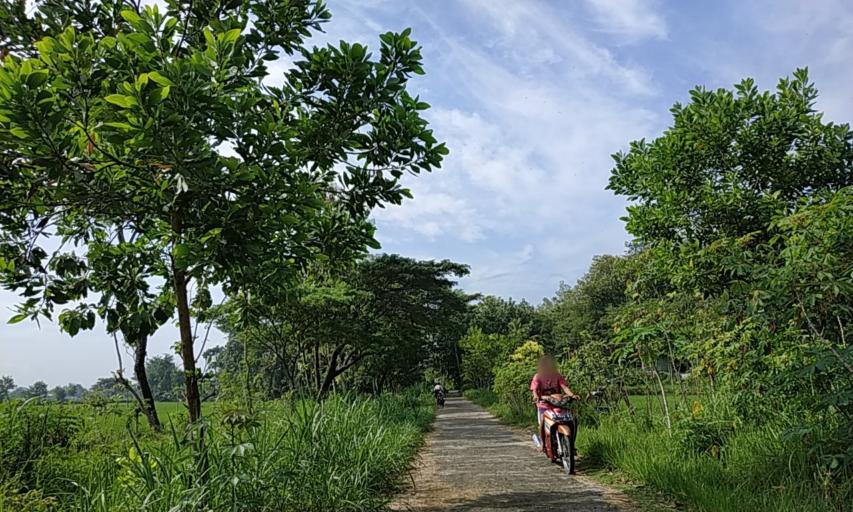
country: ID
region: Central Java
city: Trucuk
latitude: -7.7636
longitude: 110.6811
